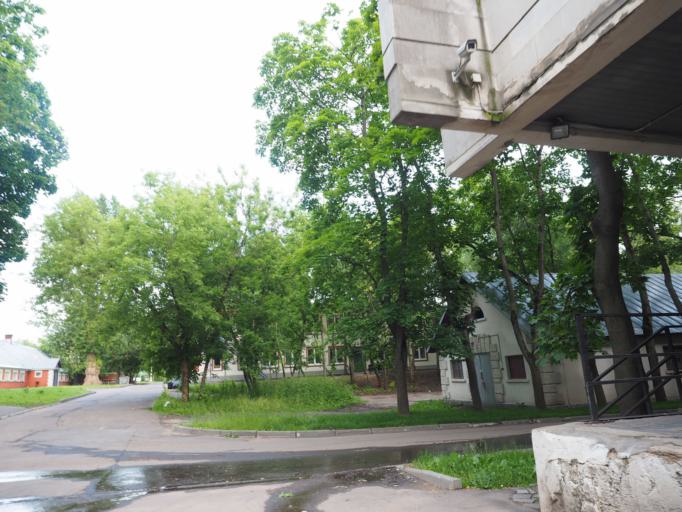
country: RU
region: Moscow
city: Sviblovo
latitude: 55.8384
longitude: 37.6286
